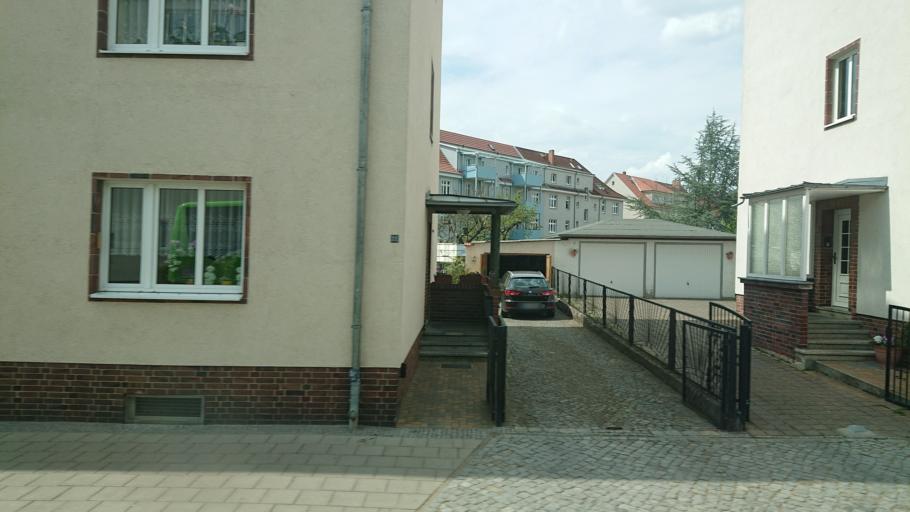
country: DE
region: Mecklenburg-Vorpommern
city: Neustrelitz
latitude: 53.3619
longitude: 13.0738
